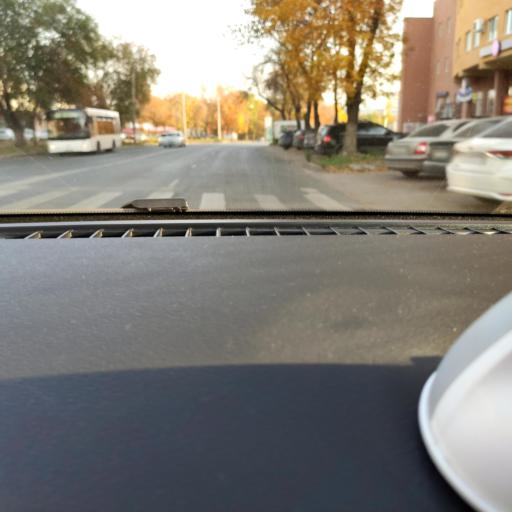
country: RU
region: Samara
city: Samara
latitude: 53.2503
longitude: 50.2398
